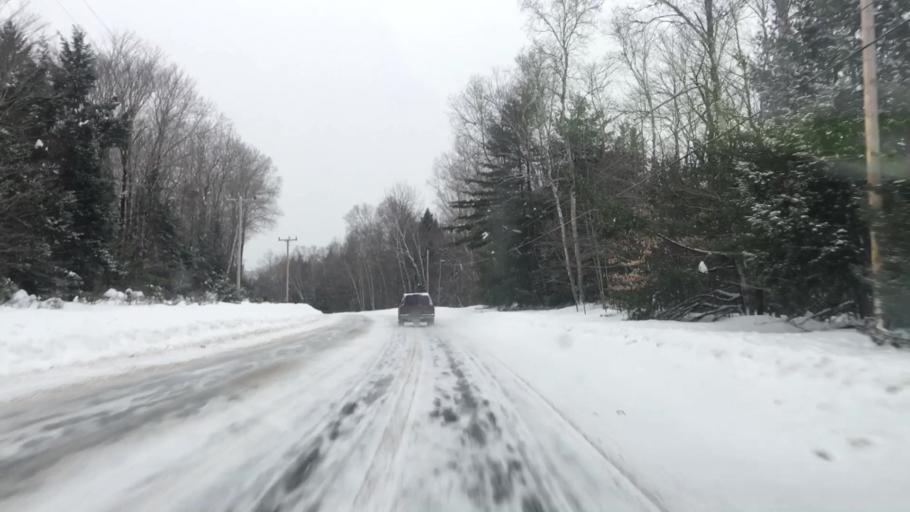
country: US
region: Maine
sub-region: Penobscot County
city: Medway
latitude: 45.5988
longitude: -68.4604
